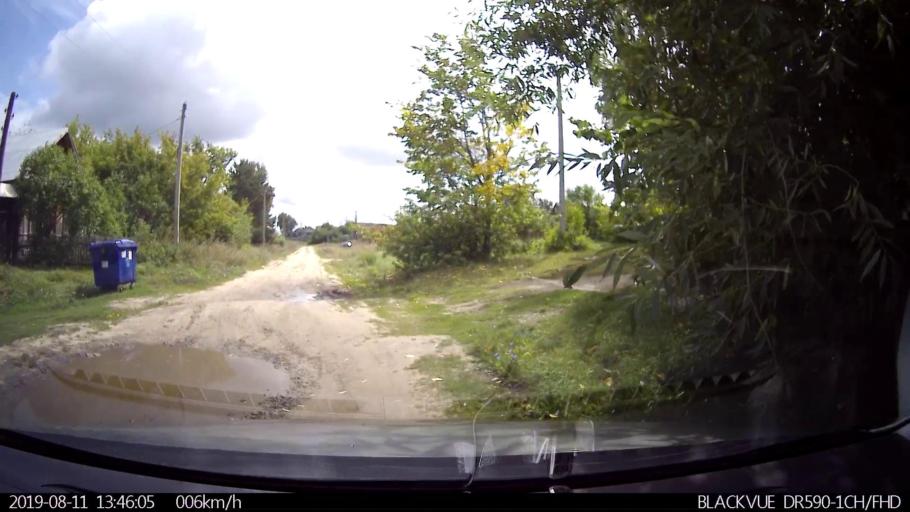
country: RU
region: Ulyanovsk
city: Ignatovka
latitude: 53.8517
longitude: 47.5750
